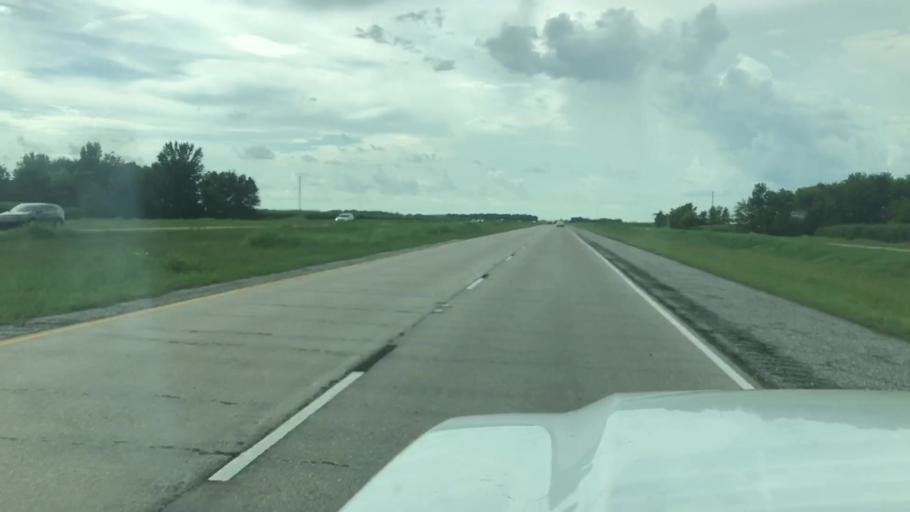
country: US
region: Louisiana
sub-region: Saint Mary Parish
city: Baldwin
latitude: 29.8462
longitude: -91.5873
